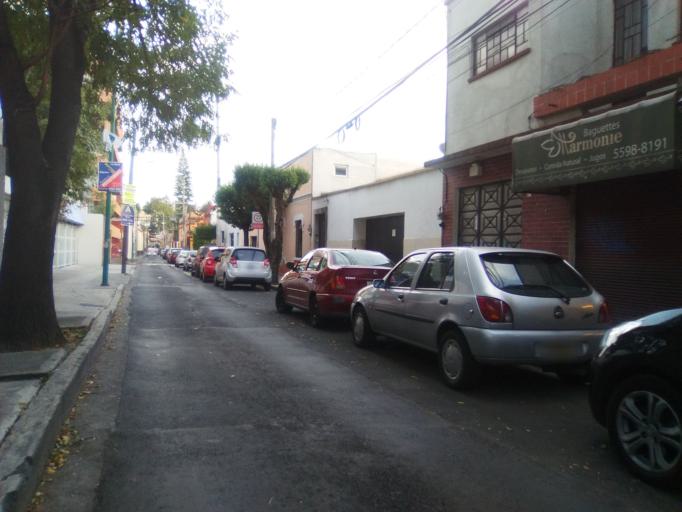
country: MX
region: Mexico City
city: Colonia del Valle
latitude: 19.3781
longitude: -99.1846
